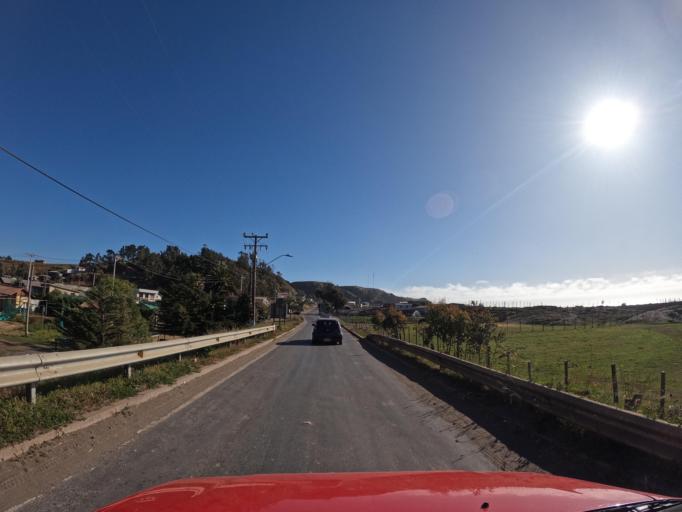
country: CL
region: Maule
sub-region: Provincia de Talca
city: Constitucion
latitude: -34.8804
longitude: -72.1559
